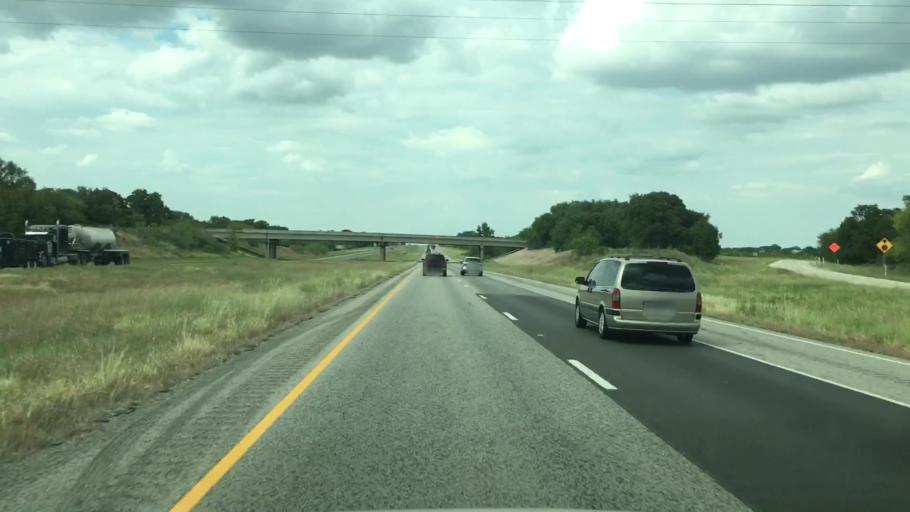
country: US
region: Texas
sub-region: Atascosa County
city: Pleasanton
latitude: 29.0494
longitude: -98.4318
